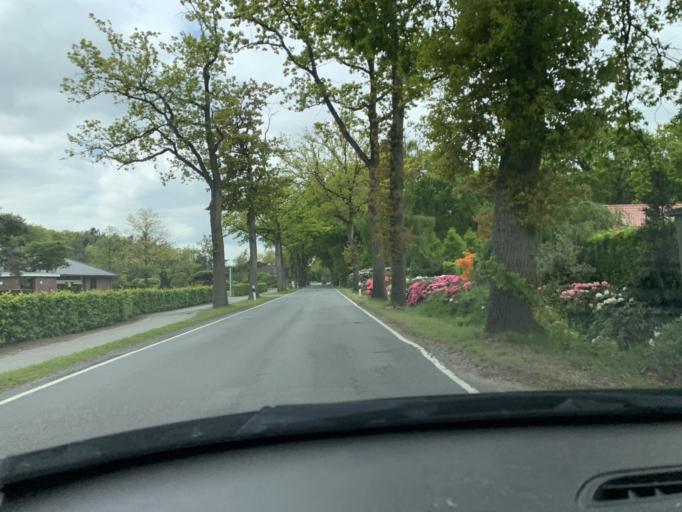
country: DE
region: Lower Saxony
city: Westerstede
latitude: 53.2350
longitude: 7.9759
